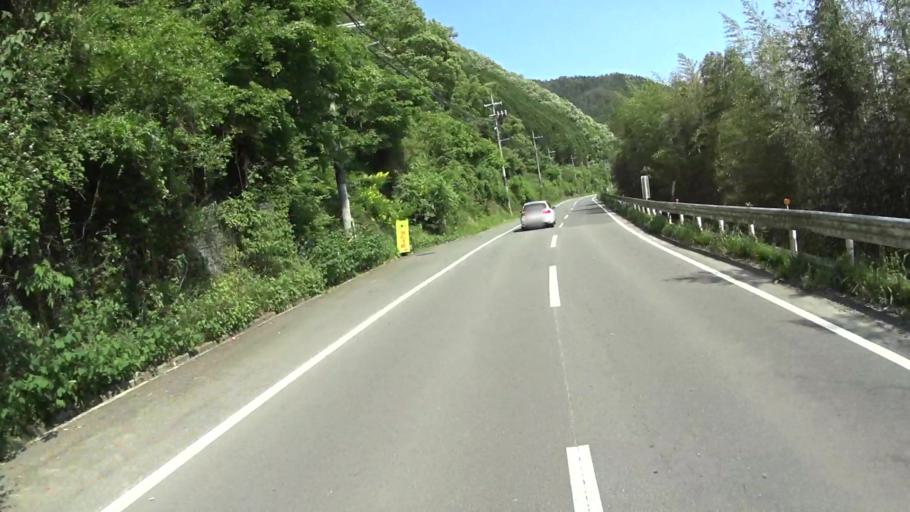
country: JP
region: Kyoto
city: Kameoka
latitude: 35.1189
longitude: 135.5147
